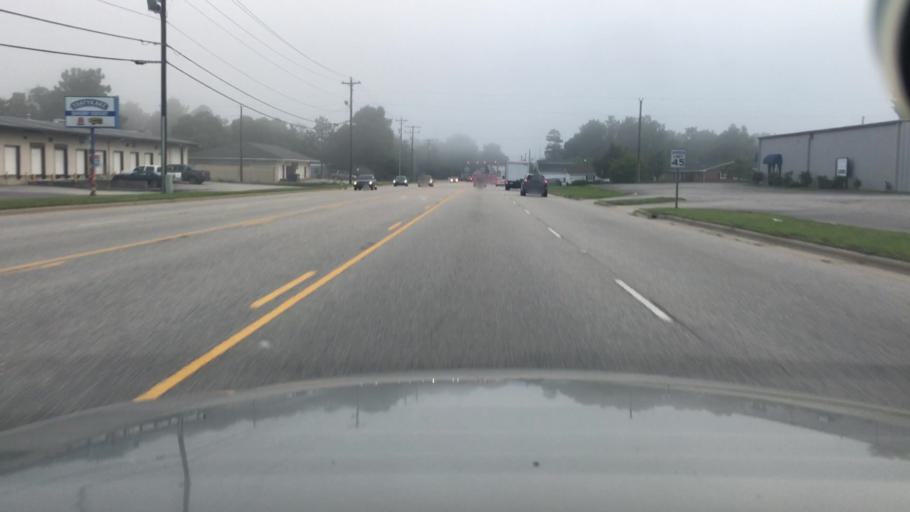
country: US
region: North Carolina
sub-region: Cumberland County
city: Hope Mills
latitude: 35.0154
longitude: -78.9187
